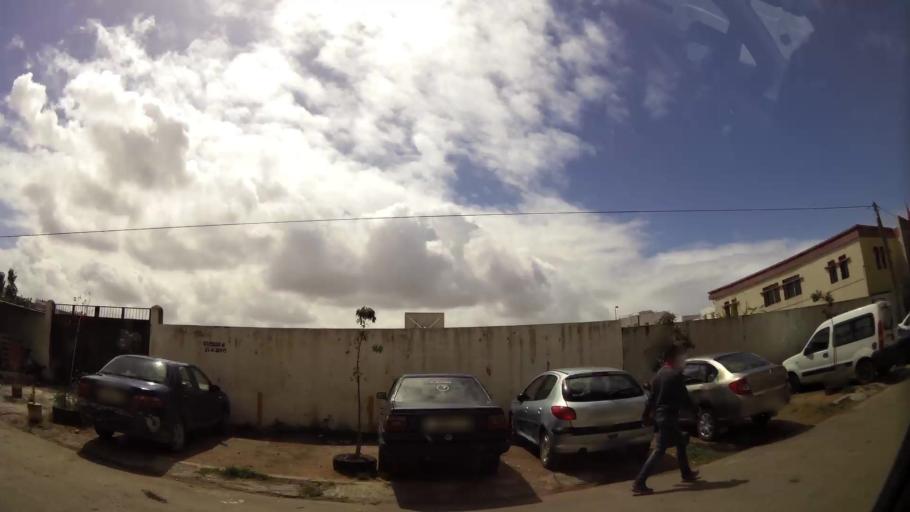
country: MA
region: Grand Casablanca
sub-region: Mediouna
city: Tit Mellil
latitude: 33.6015
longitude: -7.4807
